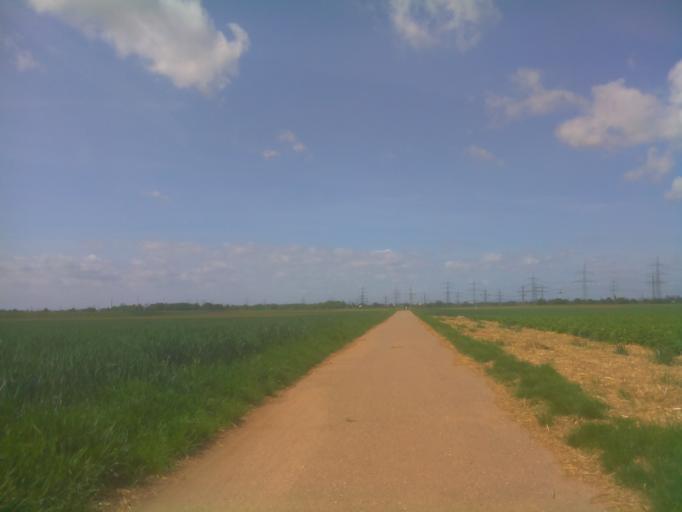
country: DE
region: Baden-Wuerttemberg
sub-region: Karlsruhe Region
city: Ilvesheim
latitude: 49.4975
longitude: 8.5787
